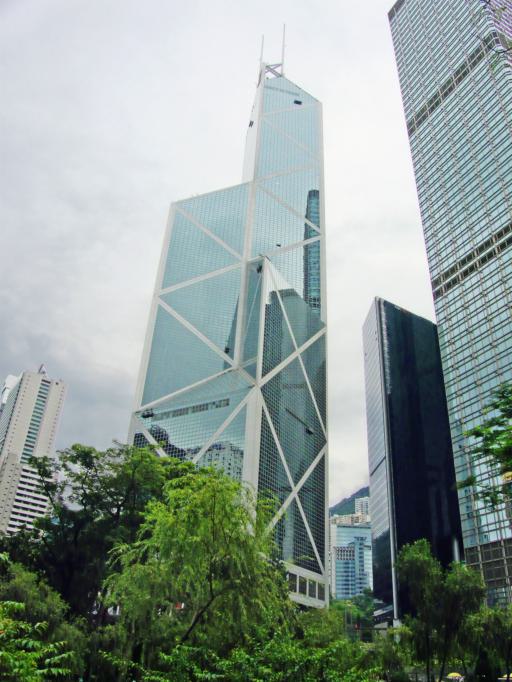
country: HK
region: Central and Western
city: Central
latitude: 22.2807
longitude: 114.1610
